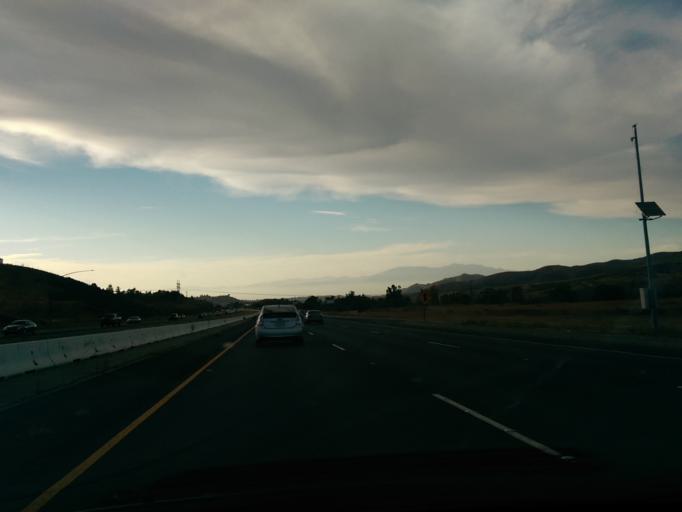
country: US
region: California
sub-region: Riverside County
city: El Cerrito
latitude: 33.7786
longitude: -117.4883
